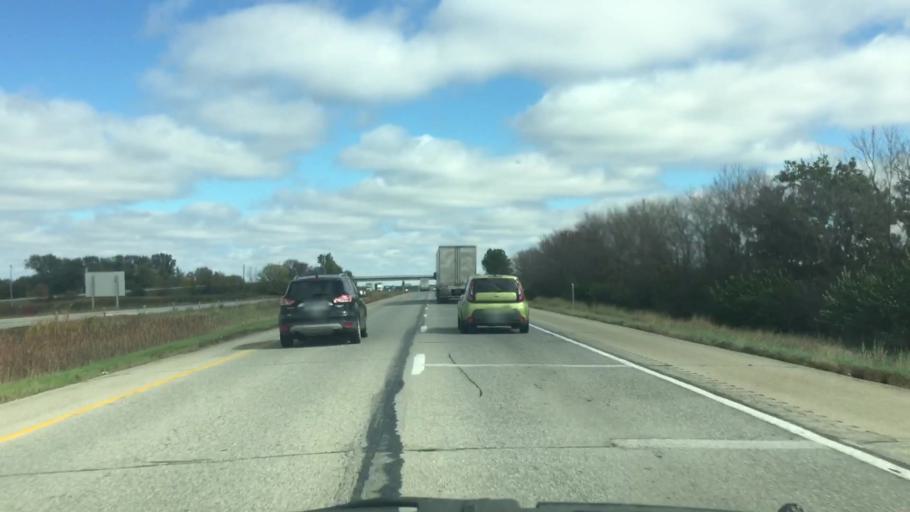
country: US
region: Iowa
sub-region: Jasper County
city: Newton
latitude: 41.6855
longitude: -92.8860
